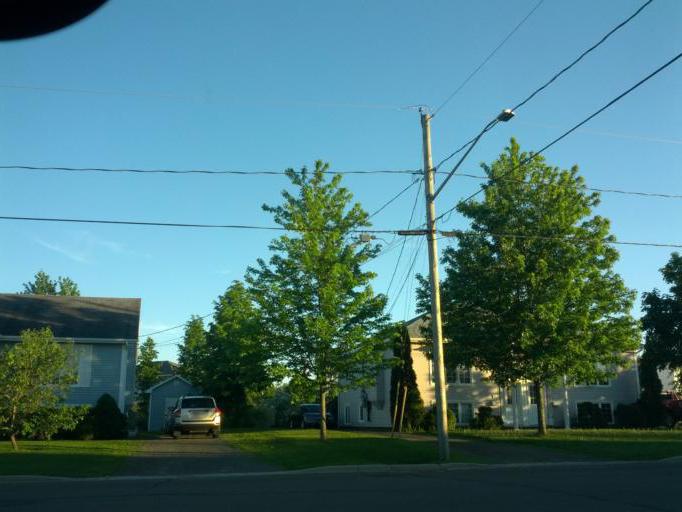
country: CA
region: New Brunswick
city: Moncton
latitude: 46.1192
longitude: -64.8514
